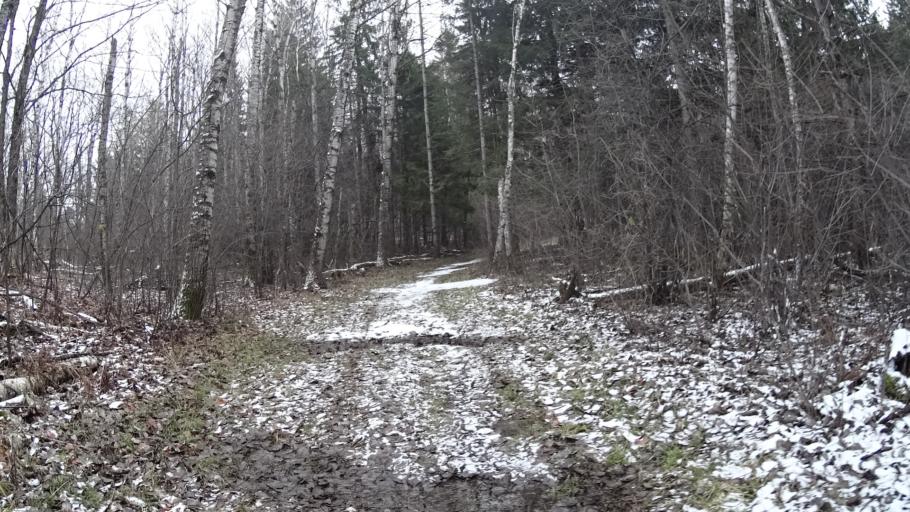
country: US
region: Minnesota
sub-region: Saint Louis County
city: Arnold
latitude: 46.8361
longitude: -92.0842
